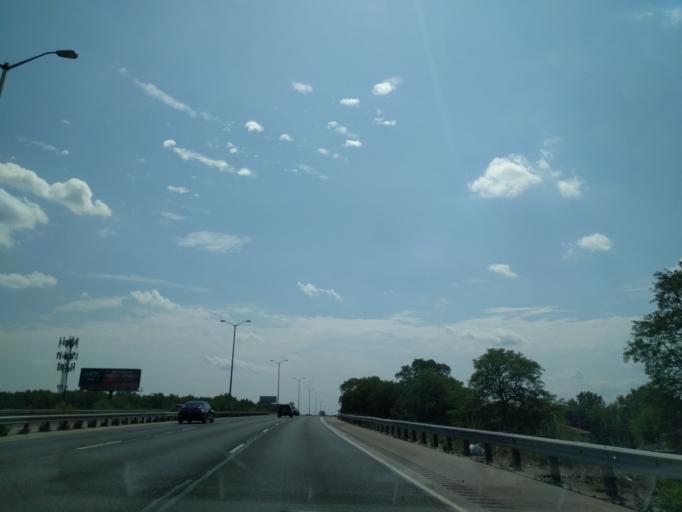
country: US
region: Illinois
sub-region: Cook County
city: South Holland
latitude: 41.6109
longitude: -87.5798
